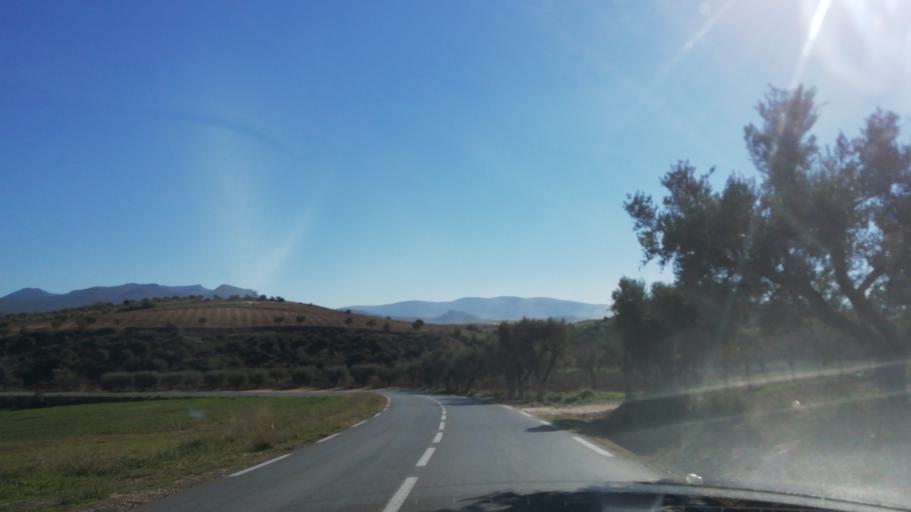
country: DZ
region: Tlemcen
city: Beni Mester
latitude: 34.8270
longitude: -1.5777
